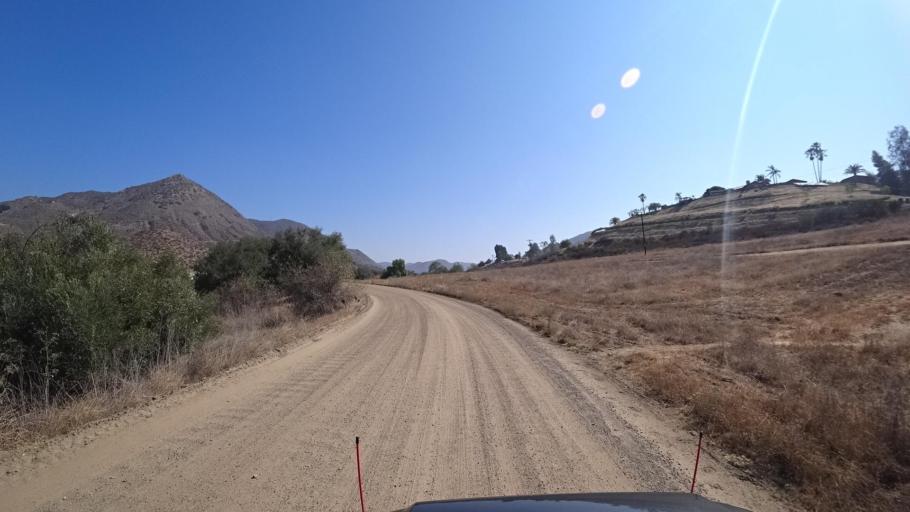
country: US
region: California
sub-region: San Diego County
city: Fallbrook
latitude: 33.4138
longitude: -117.2135
